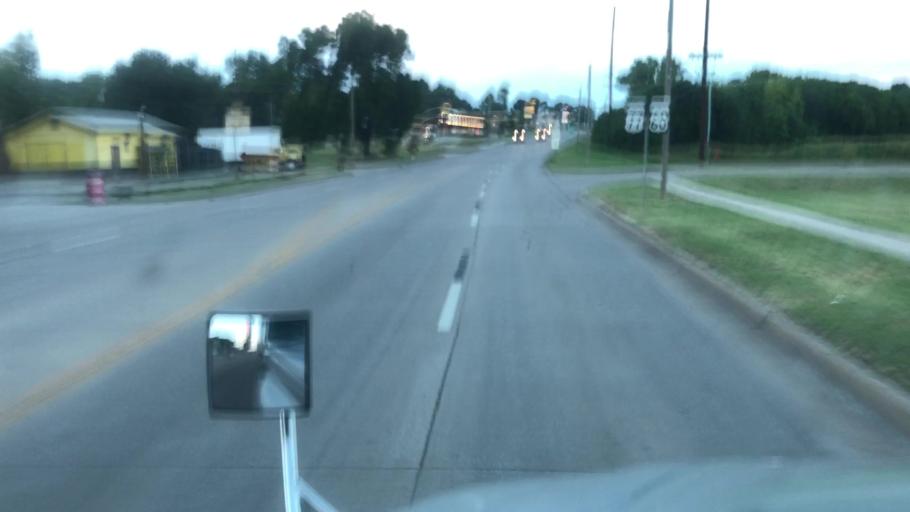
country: US
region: Oklahoma
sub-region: Kay County
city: Ponca City
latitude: 36.6957
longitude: -97.0671
